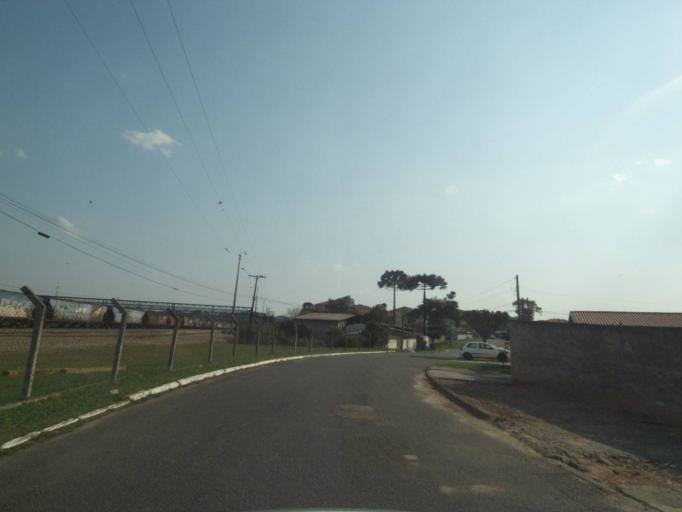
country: BR
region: Parana
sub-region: Sao Jose Dos Pinhais
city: Sao Jose dos Pinhais
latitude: -25.5350
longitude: -49.2339
